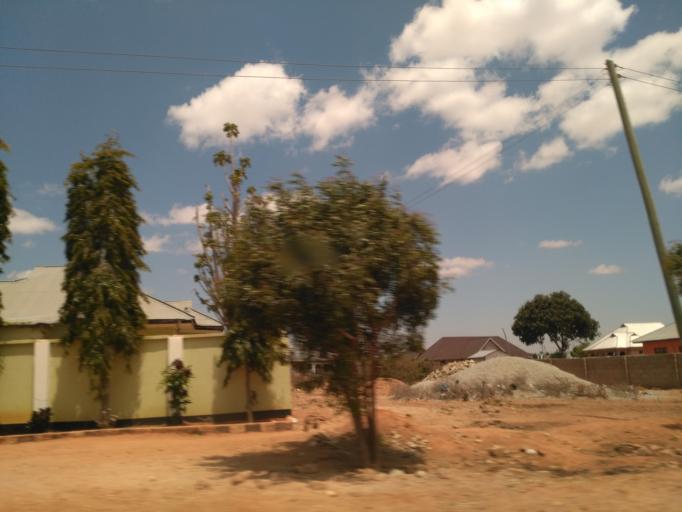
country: TZ
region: Dodoma
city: Kisasa
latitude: -6.1720
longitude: 35.8003
